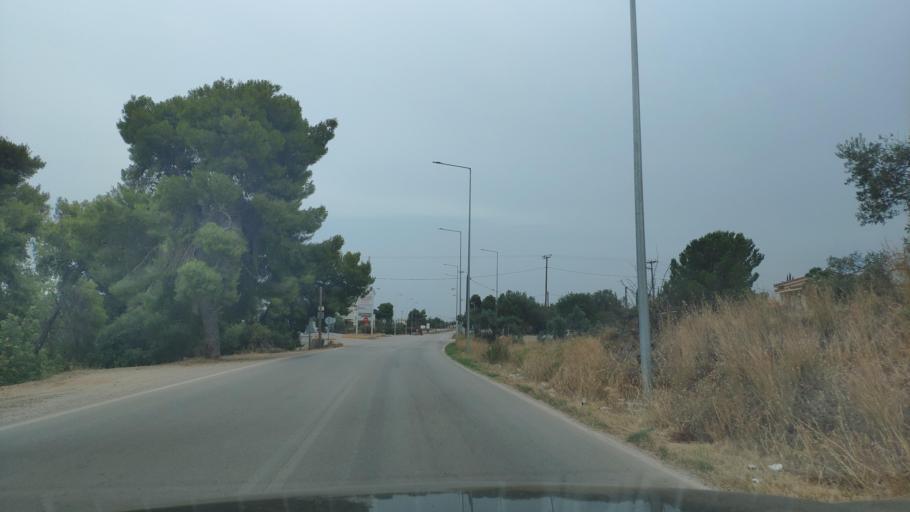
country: GR
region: Peloponnese
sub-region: Nomos Argolidos
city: Porto Cheli
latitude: 37.3494
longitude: 23.1572
